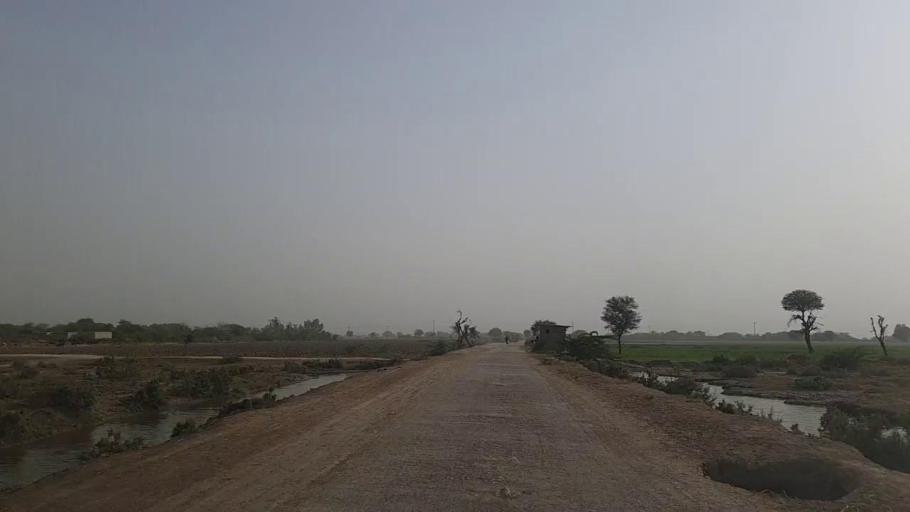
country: PK
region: Sindh
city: Pithoro
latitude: 25.4033
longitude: 69.2637
